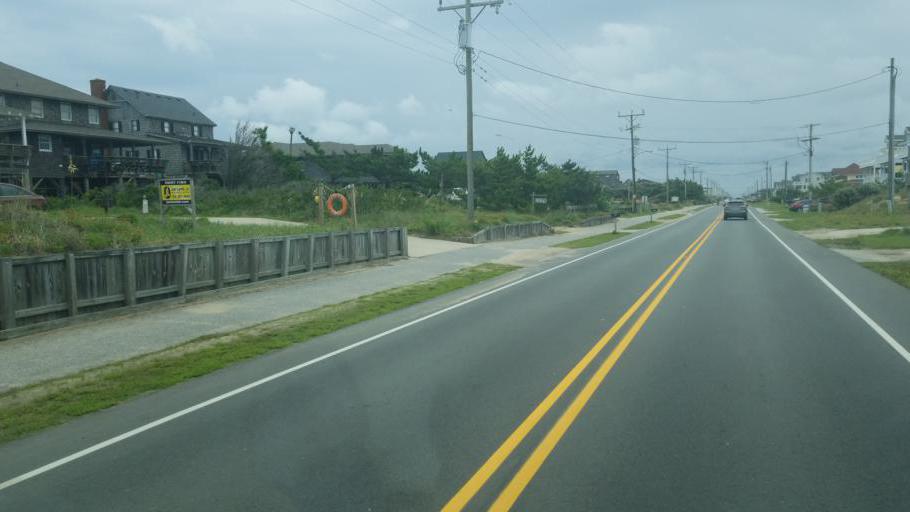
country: US
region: North Carolina
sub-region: Dare County
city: Nags Head
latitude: 35.9525
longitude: -75.6214
